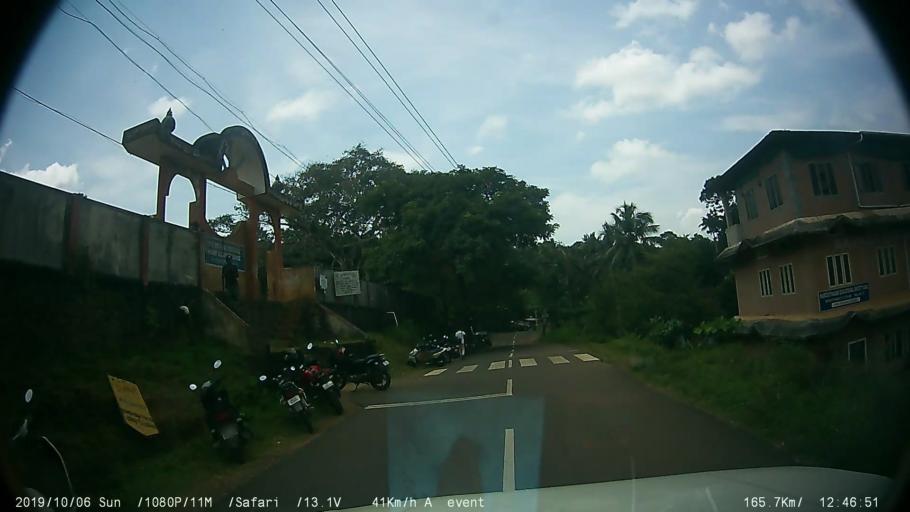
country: IN
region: Kerala
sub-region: Kottayam
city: Palackattumala
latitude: 9.7724
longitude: 76.6049
